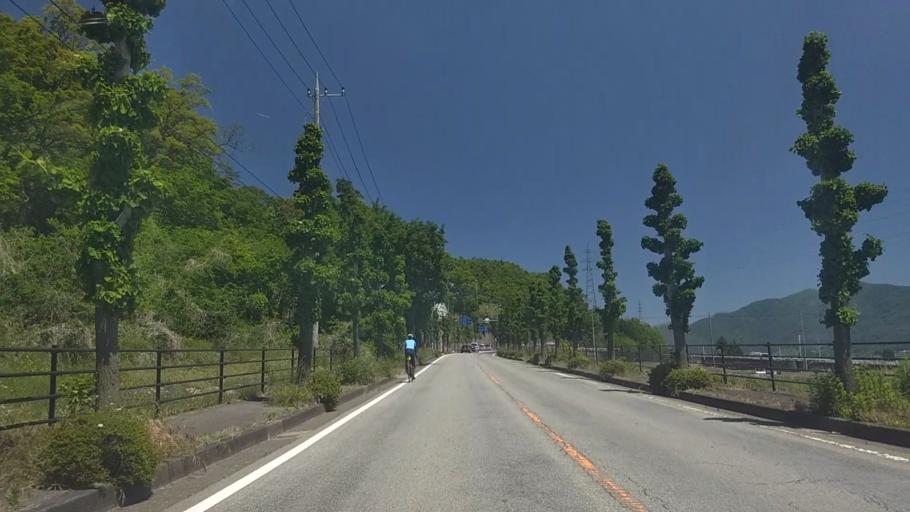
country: JP
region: Yamanashi
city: Nirasaki
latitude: 35.7994
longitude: 138.4250
